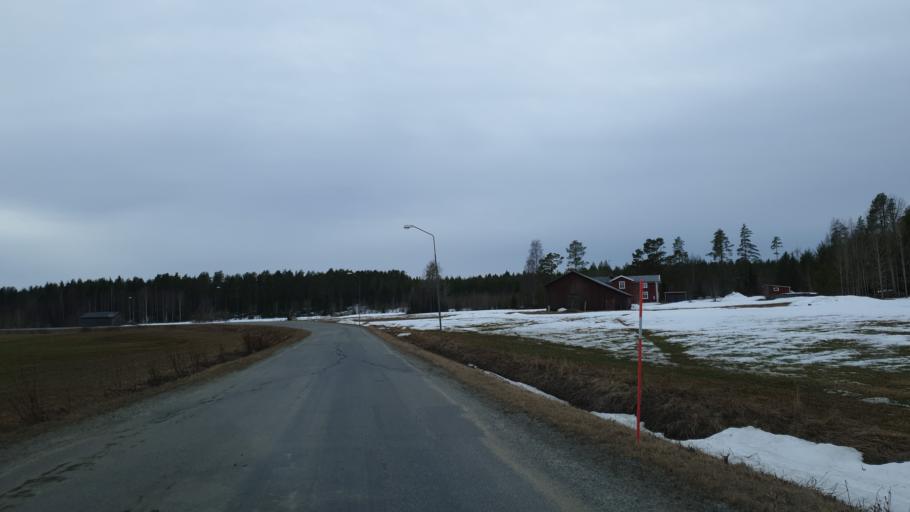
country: SE
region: Vaesterbotten
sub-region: Robertsfors Kommun
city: Robertsfors
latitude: 64.4006
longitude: 21.0052
